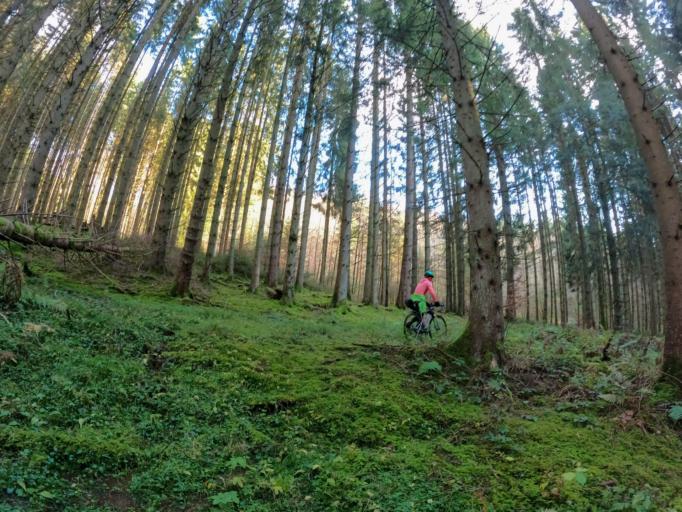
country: LU
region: Diekirch
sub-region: Canton de Wiltz
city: Bavigne
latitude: 49.9734
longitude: 5.8211
